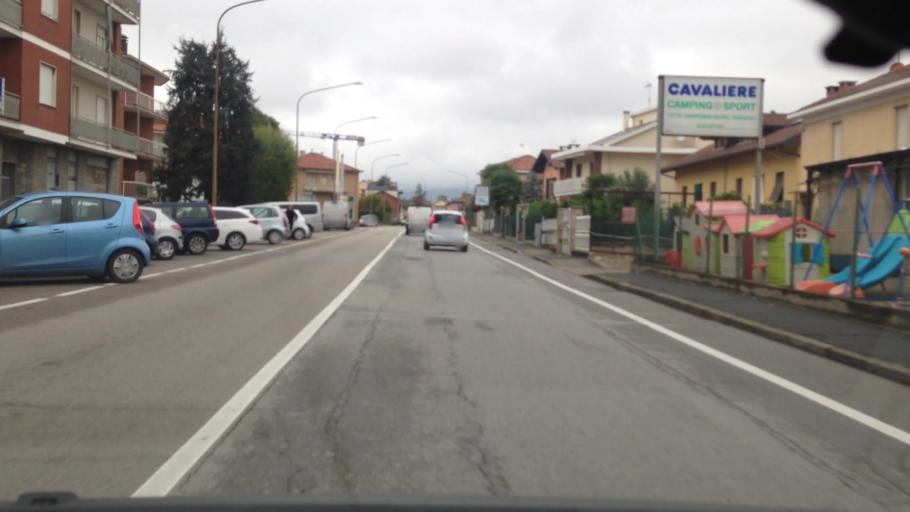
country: IT
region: Piedmont
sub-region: Provincia di Torino
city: Chieri
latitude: 45.0045
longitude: 7.8380
